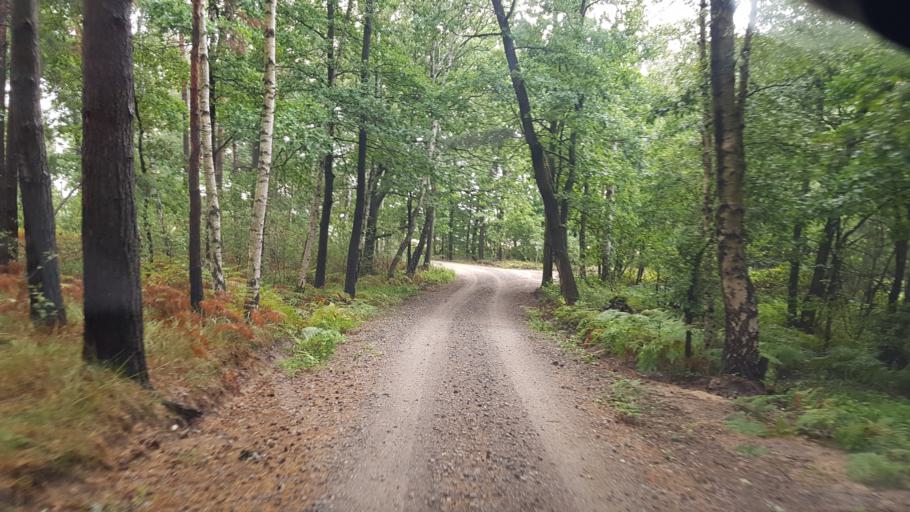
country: DE
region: Brandenburg
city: Ruckersdorf
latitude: 51.5556
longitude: 13.5717
